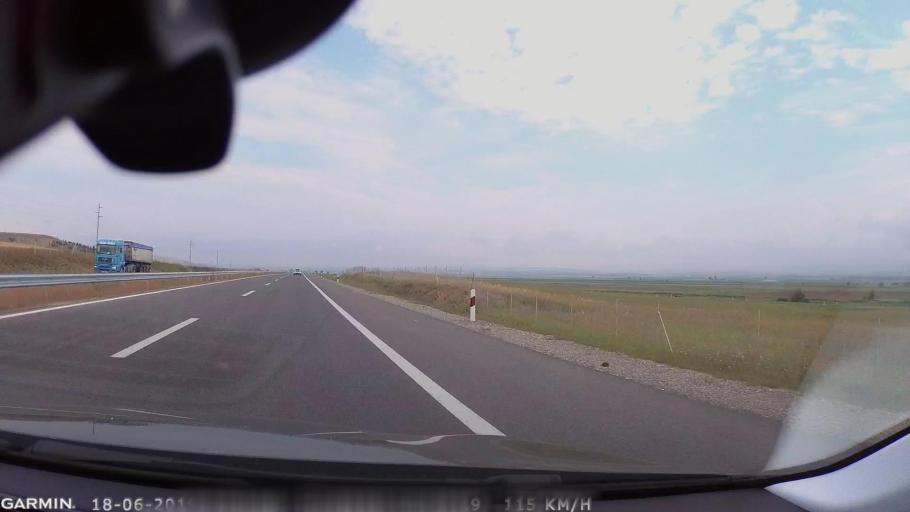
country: MK
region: Stip
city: Shtip
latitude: 41.8024
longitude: 22.0741
